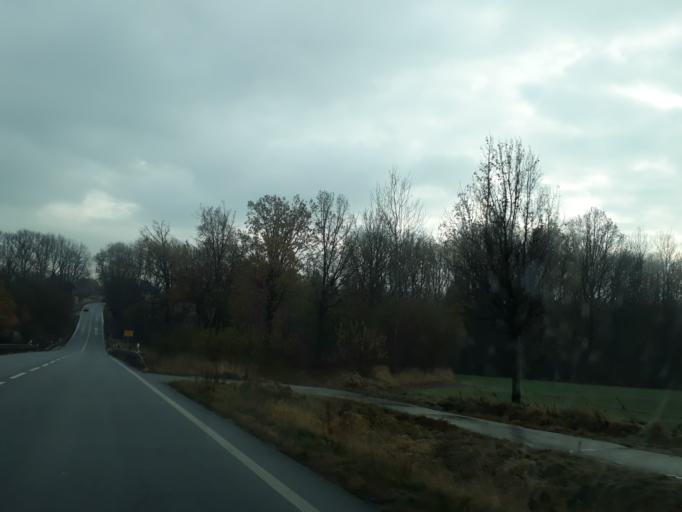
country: DE
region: Saxony
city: Lobau
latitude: 51.1199
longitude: 14.6391
